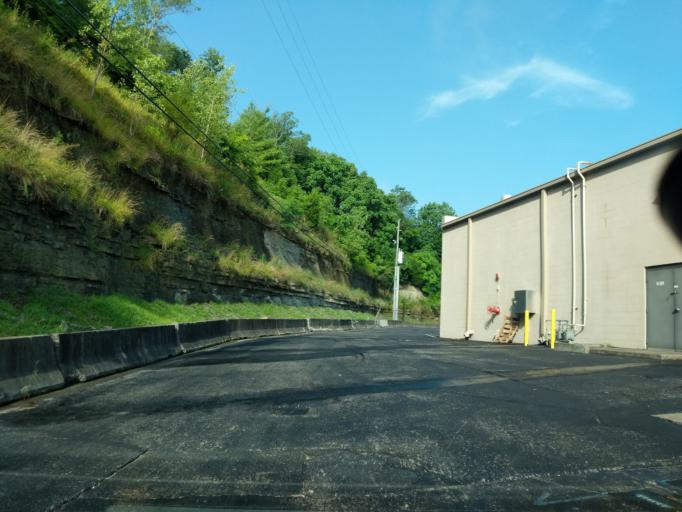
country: US
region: Tennessee
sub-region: Davidson County
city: Goodlettsville
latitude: 36.3058
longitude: -86.6829
